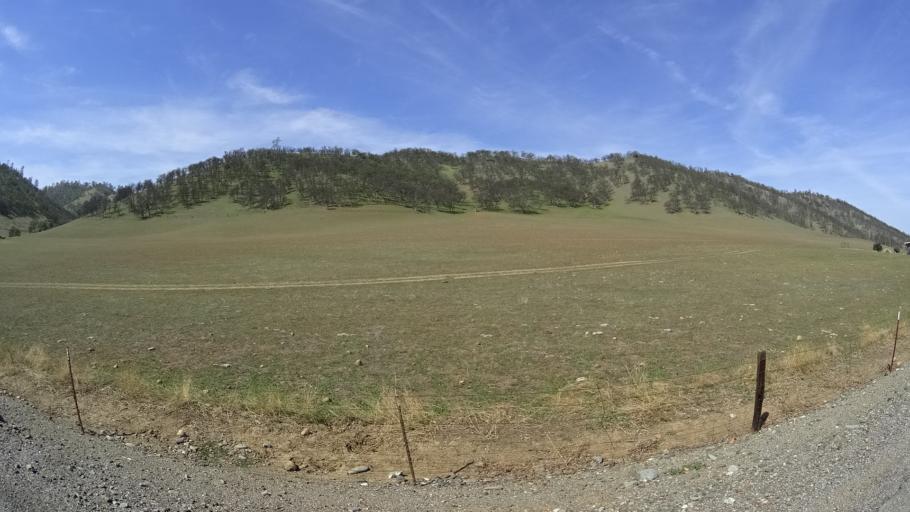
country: US
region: California
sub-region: Glenn County
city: Willows
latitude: 39.5179
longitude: -122.4562
